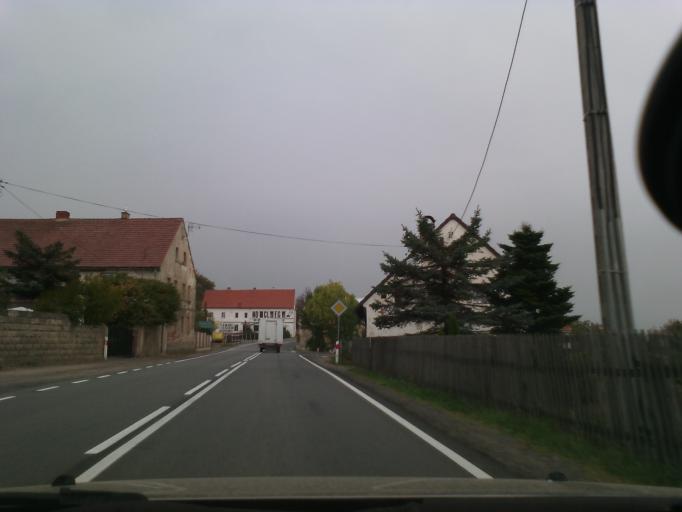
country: PL
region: Lower Silesian Voivodeship
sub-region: Powiat swidnicki
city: Swiebodzice
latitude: 50.8946
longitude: 16.2604
